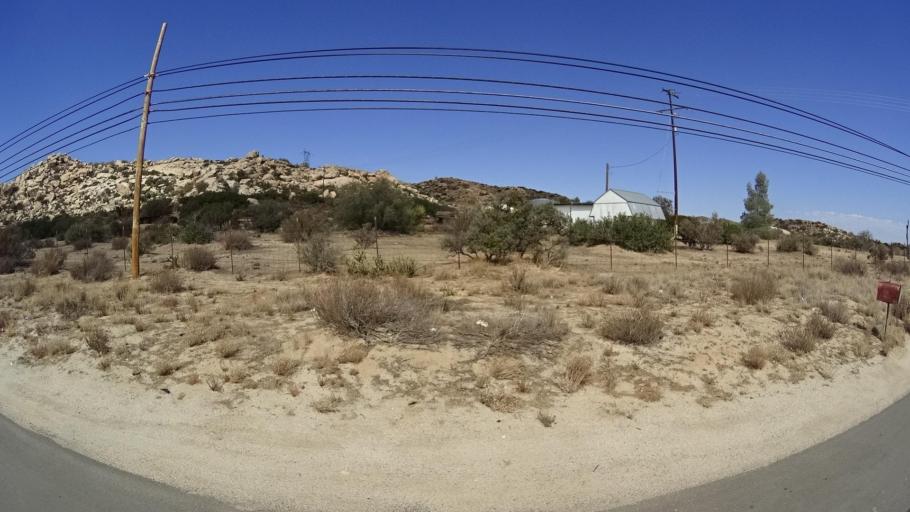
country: MX
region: Baja California
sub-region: Tecate
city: Cereso del Hongo
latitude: 32.6443
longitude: -116.2349
